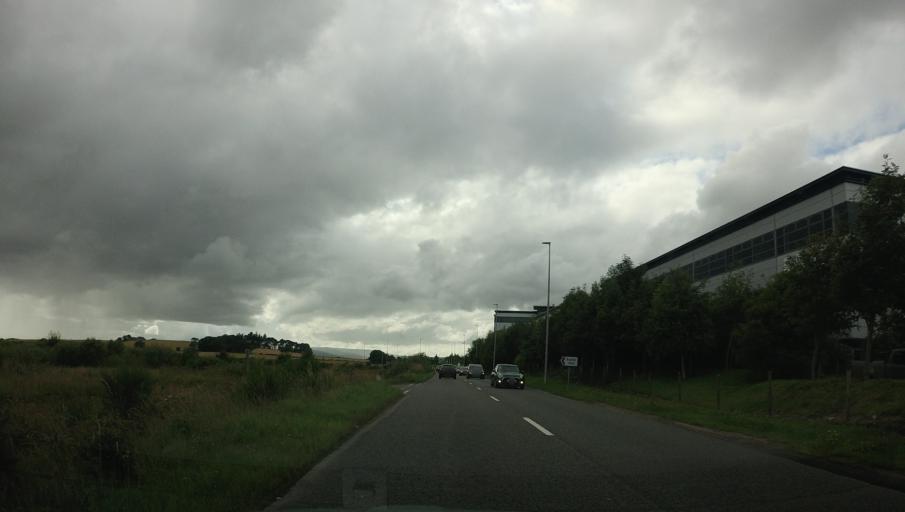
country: GB
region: Scotland
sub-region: Aberdeenshire
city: Westhill
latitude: 57.1445
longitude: -2.2794
